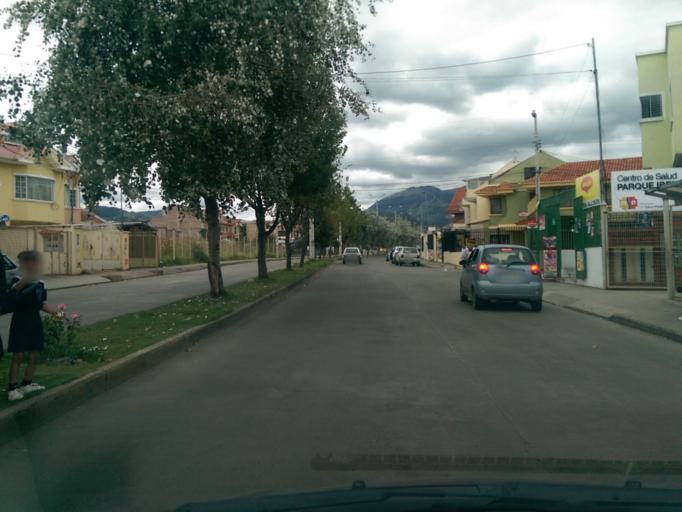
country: EC
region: Azuay
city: Cuenca
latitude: -2.9101
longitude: -79.0242
